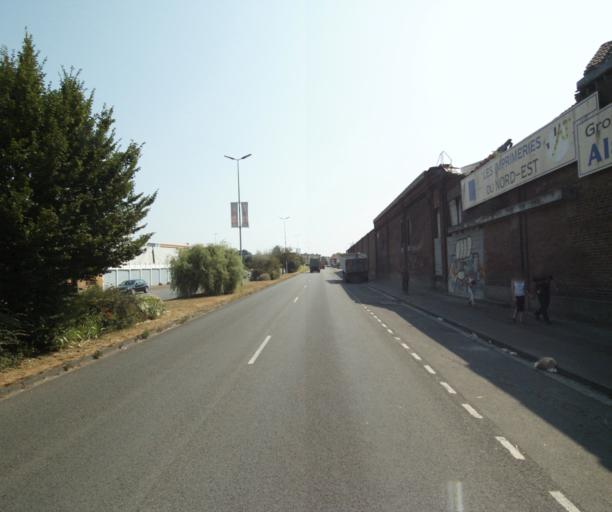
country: FR
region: Nord-Pas-de-Calais
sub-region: Departement du Nord
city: Neuville-en-Ferrain
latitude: 50.7374
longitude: 3.1583
